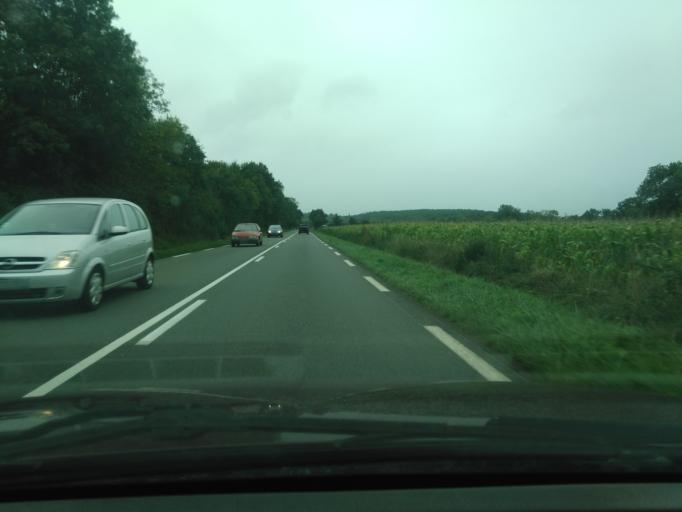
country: FR
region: Pays de la Loire
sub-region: Departement de la Vendee
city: Sainte-Hermine
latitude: 46.5796
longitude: -1.1089
